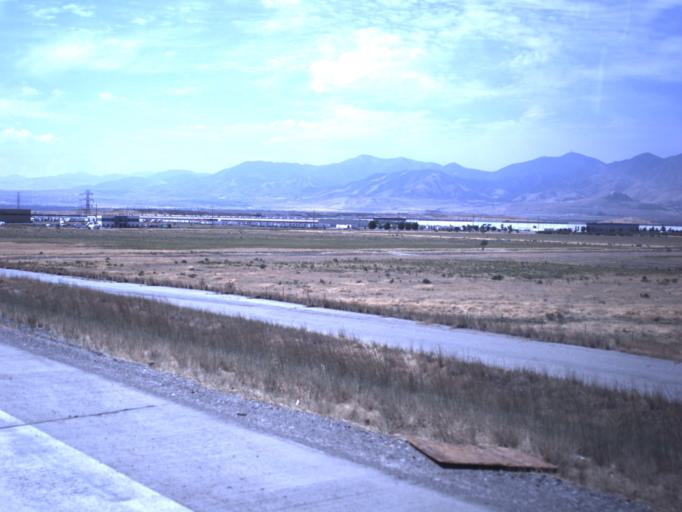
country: US
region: Utah
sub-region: Salt Lake County
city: West Valley City
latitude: 40.7677
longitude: -112.0251
